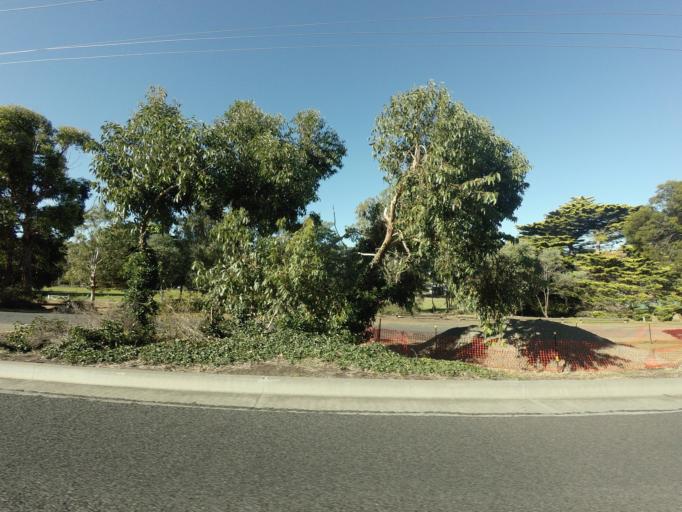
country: AU
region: Tasmania
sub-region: Clarence
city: Bellerive
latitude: -42.8683
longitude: 147.3633
